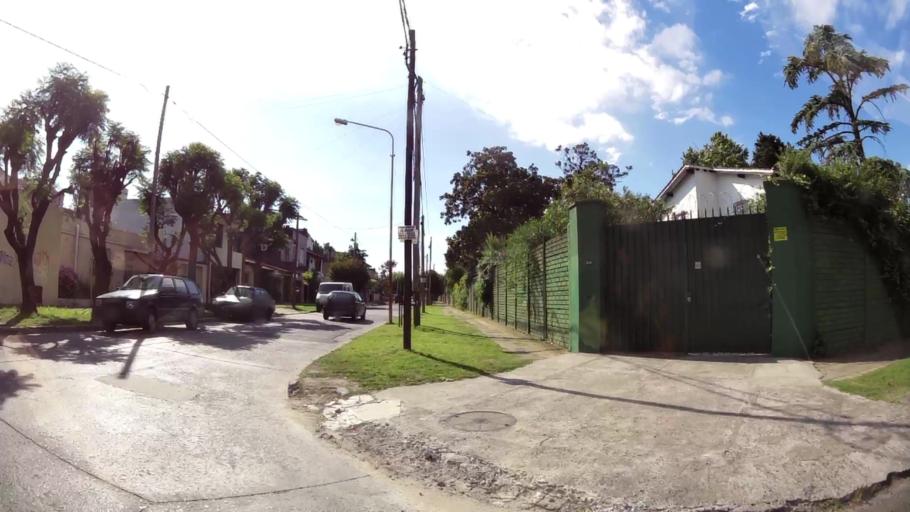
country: AR
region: Buenos Aires
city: San Justo
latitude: -34.6552
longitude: -58.5789
